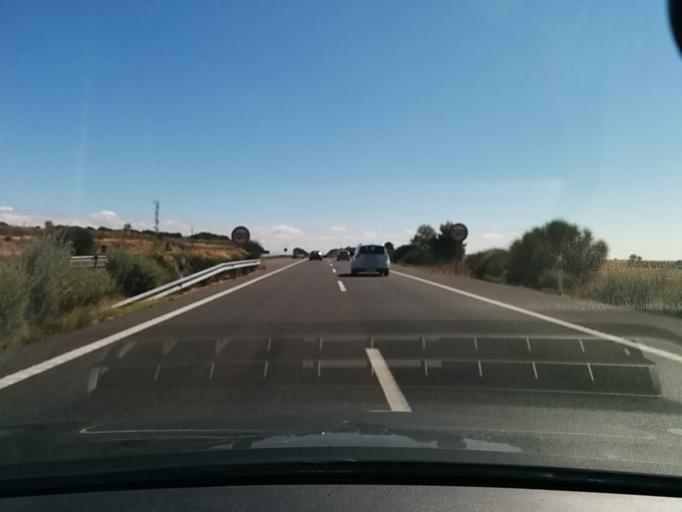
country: ES
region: Aragon
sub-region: Provincia de Huesca
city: Almudebar
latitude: 42.0685
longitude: -0.5144
